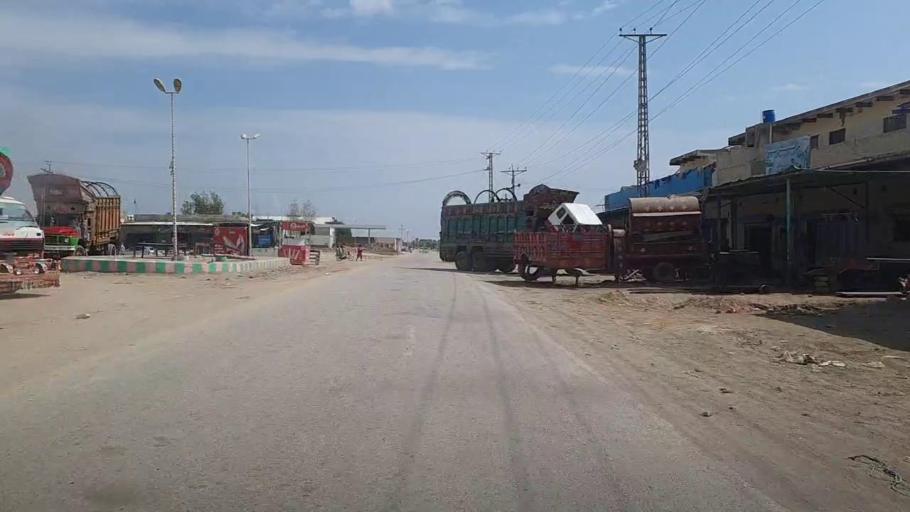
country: PK
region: Sindh
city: Thul
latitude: 28.2455
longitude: 68.7853
